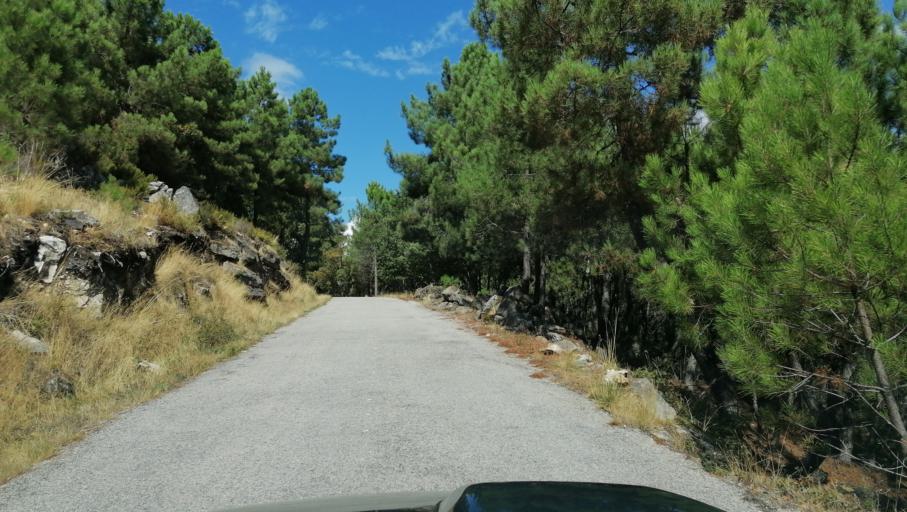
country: PT
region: Vila Real
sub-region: Vila Pouca de Aguiar
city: Vila Pouca de Aguiar
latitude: 41.5560
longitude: -7.6560
